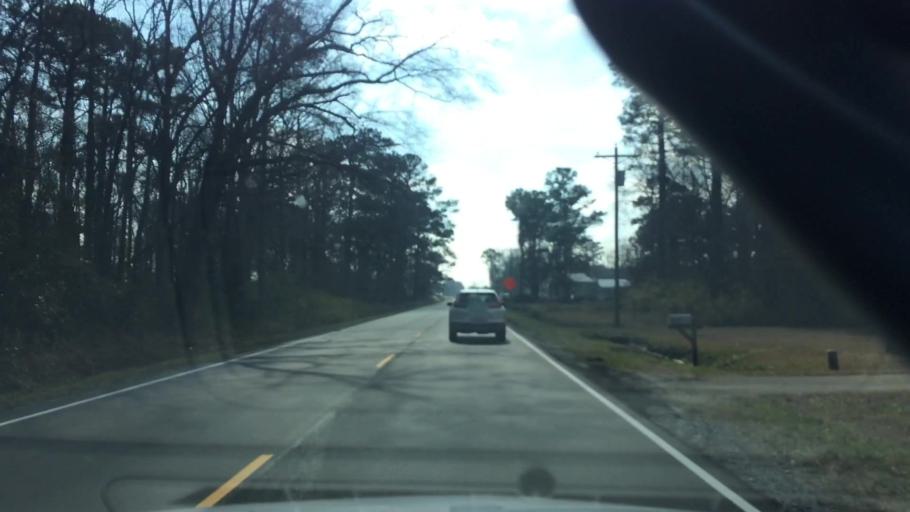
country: US
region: North Carolina
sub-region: Duplin County
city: Beulaville
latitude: 34.9633
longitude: -77.7640
